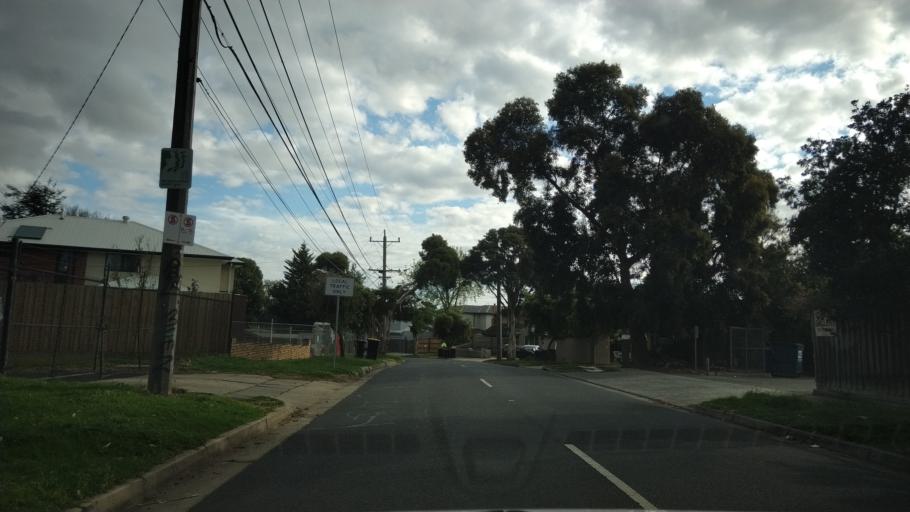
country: AU
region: Victoria
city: Highett
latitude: -37.9516
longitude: 145.0660
